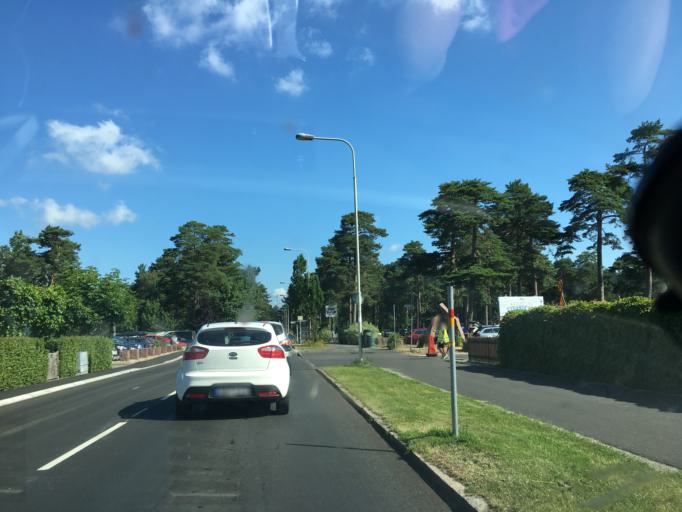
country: SE
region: Skane
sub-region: Kristianstads Kommun
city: Ahus
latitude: 55.9359
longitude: 14.3157
